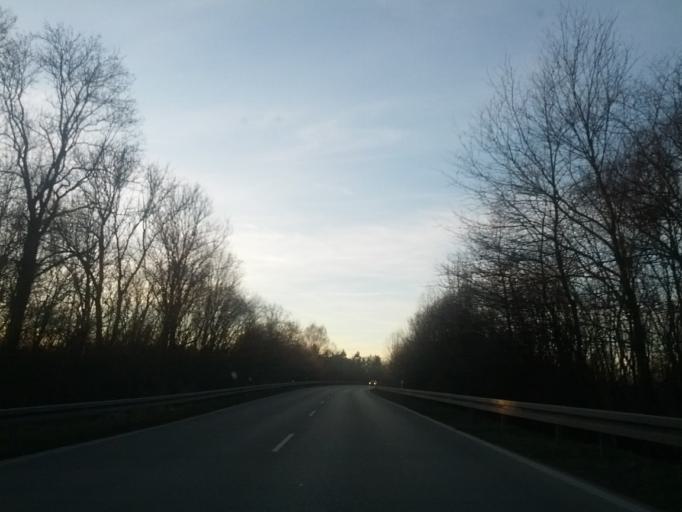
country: DE
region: Bavaria
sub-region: Swabia
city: Heimertingen
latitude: 48.0340
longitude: 10.1395
